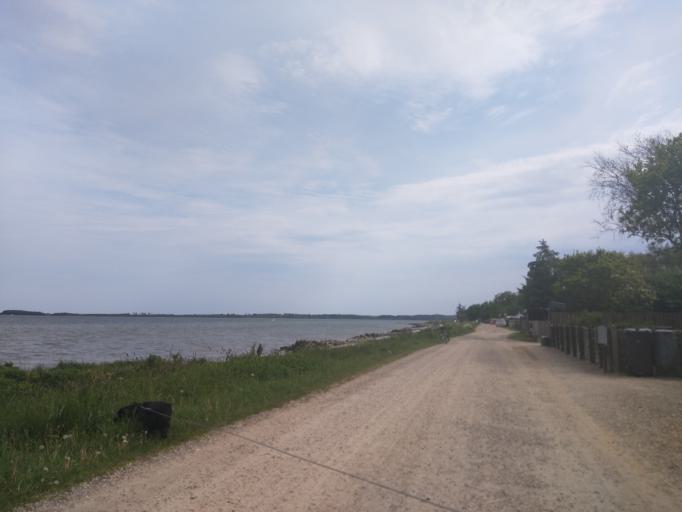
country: DK
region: North Denmark
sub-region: Morso Kommune
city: Nykobing Mors
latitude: 56.7995
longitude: 8.8775
